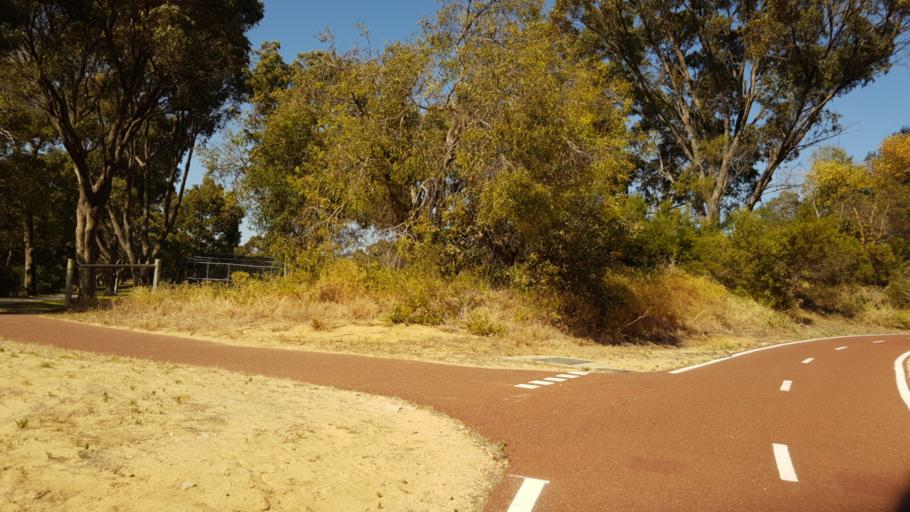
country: AU
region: Western Australia
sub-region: Stirling
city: Karrinyup
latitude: -31.8564
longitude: 115.7879
